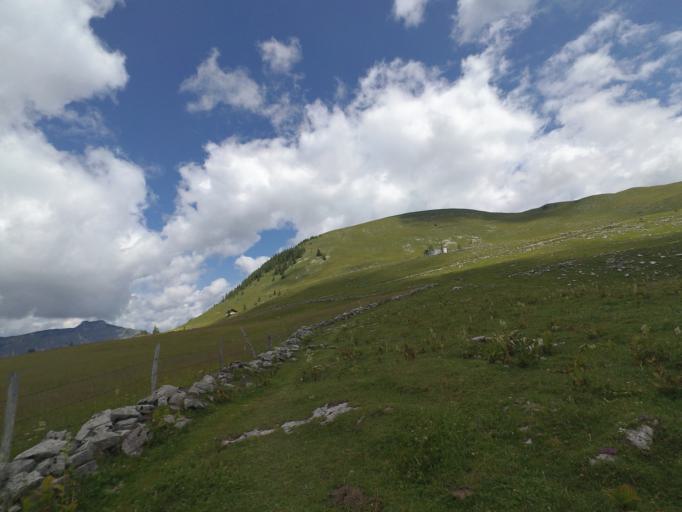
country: AT
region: Salzburg
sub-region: Politischer Bezirk Salzburg-Umgebung
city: Hintersee
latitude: 47.6500
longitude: 13.2834
